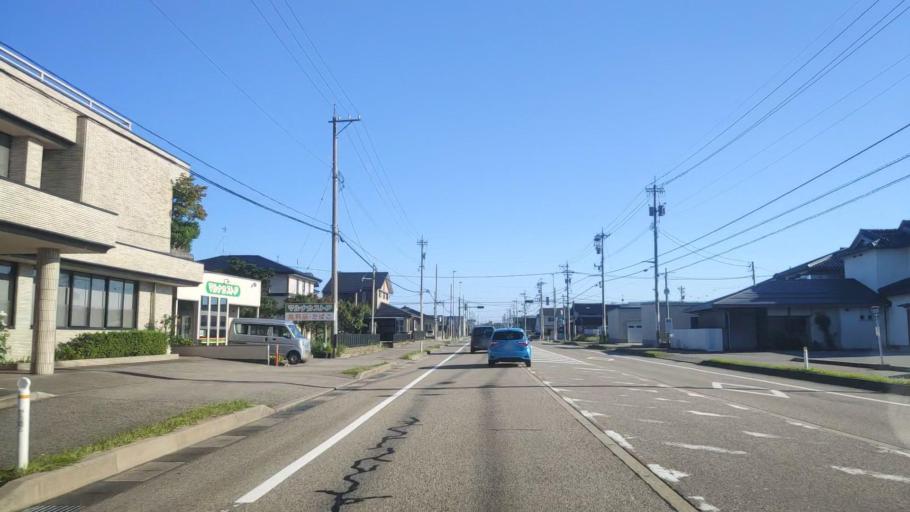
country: JP
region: Ishikawa
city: Tsubata
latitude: 36.7459
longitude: 136.7092
